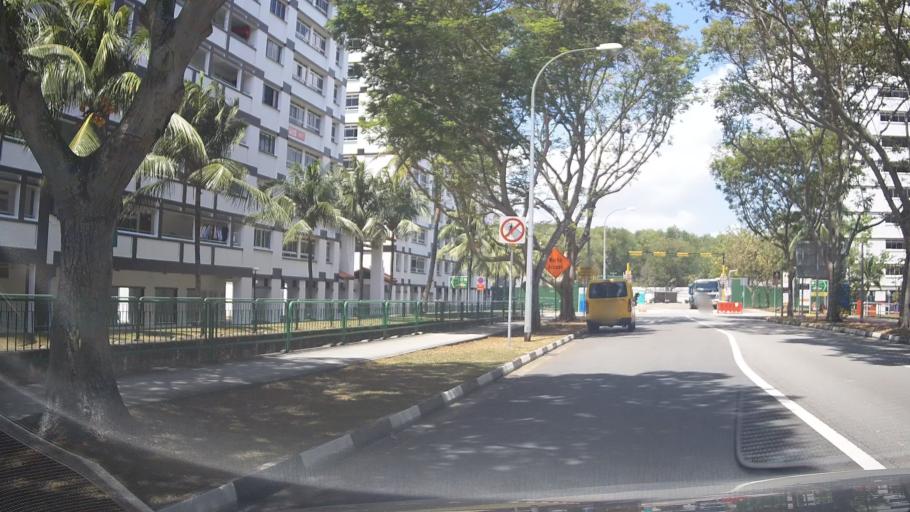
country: SG
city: Singapore
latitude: 1.3617
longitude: 103.9514
